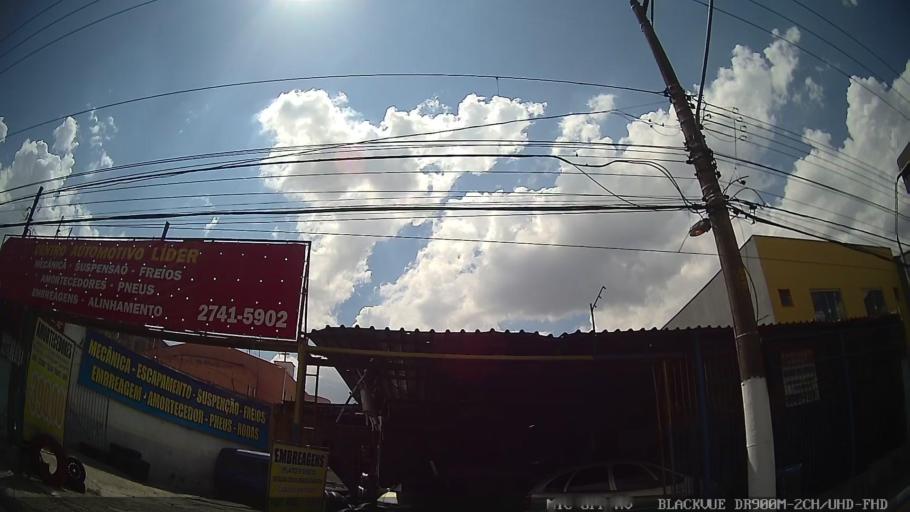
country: BR
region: Sao Paulo
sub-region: Ferraz De Vasconcelos
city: Ferraz de Vasconcelos
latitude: -23.5551
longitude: -46.4679
